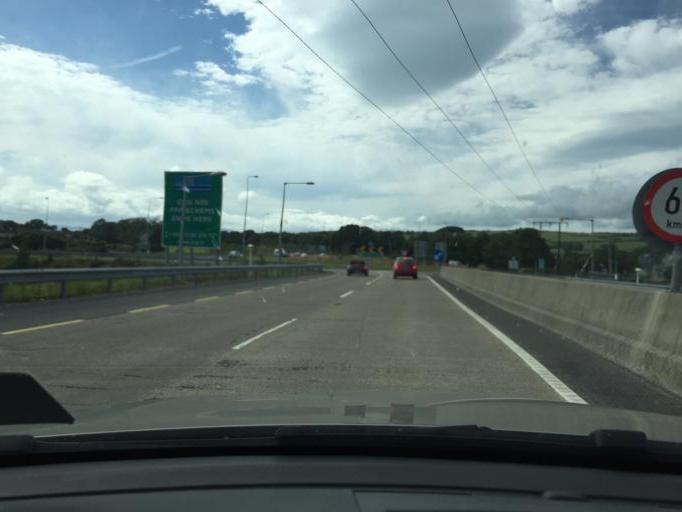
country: IE
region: Leinster
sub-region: Kilkenny
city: Mooncoin
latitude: 52.2412
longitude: -7.2462
